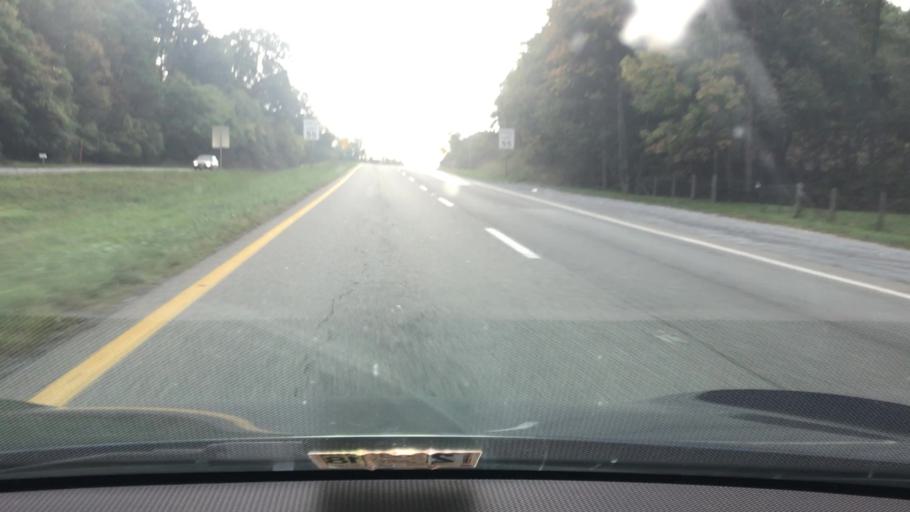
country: US
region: Virginia
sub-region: Botetourt County
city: Blue Ridge
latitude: 37.3941
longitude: -79.7467
